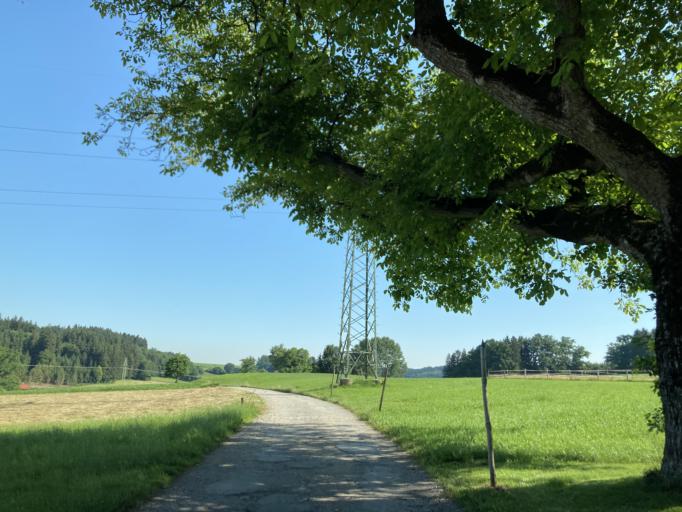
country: DE
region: Bavaria
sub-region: Upper Bavaria
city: Bad Endorf
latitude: 47.9120
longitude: 12.2816
